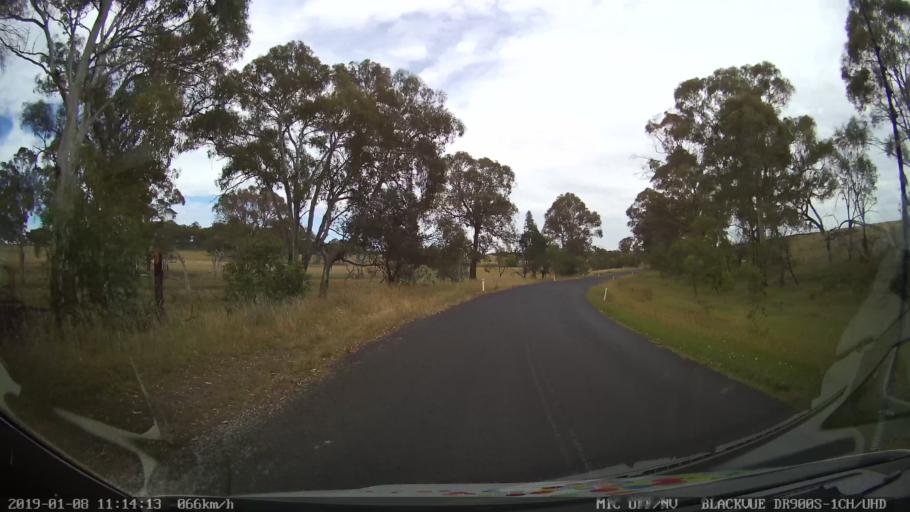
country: AU
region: New South Wales
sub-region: Guyra
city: Guyra
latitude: -30.2283
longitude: 151.5901
